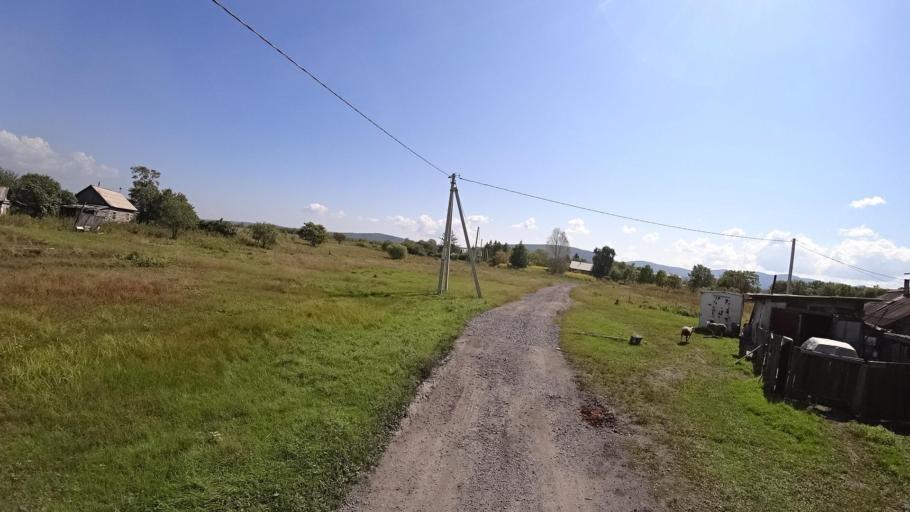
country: RU
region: Jewish Autonomous Oblast
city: Londoko
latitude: 49.0054
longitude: 131.9427
